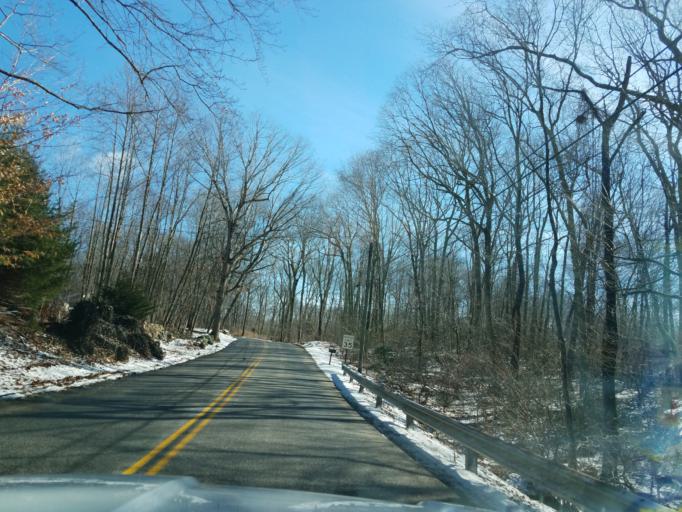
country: US
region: Connecticut
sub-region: New London County
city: Old Mystic
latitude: 41.4584
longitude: -71.9343
